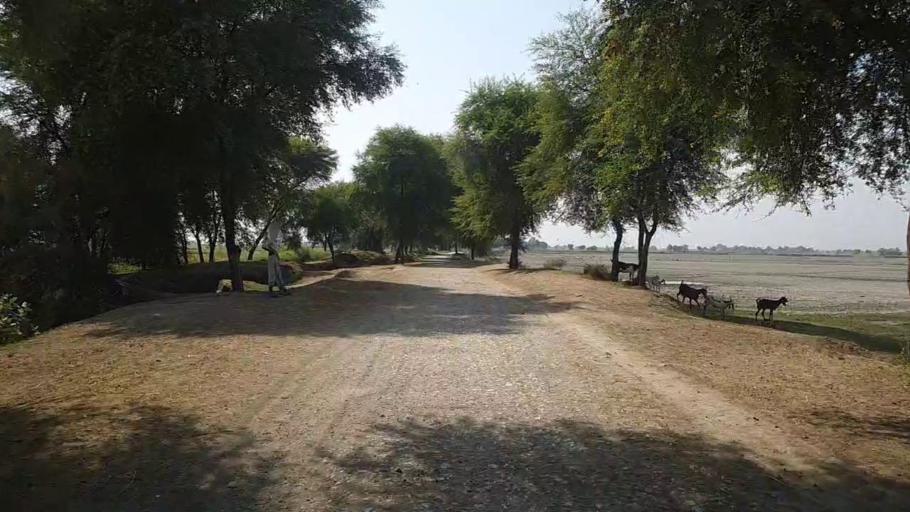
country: PK
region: Sindh
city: Kandhkot
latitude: 28.3858
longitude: 69.3182
